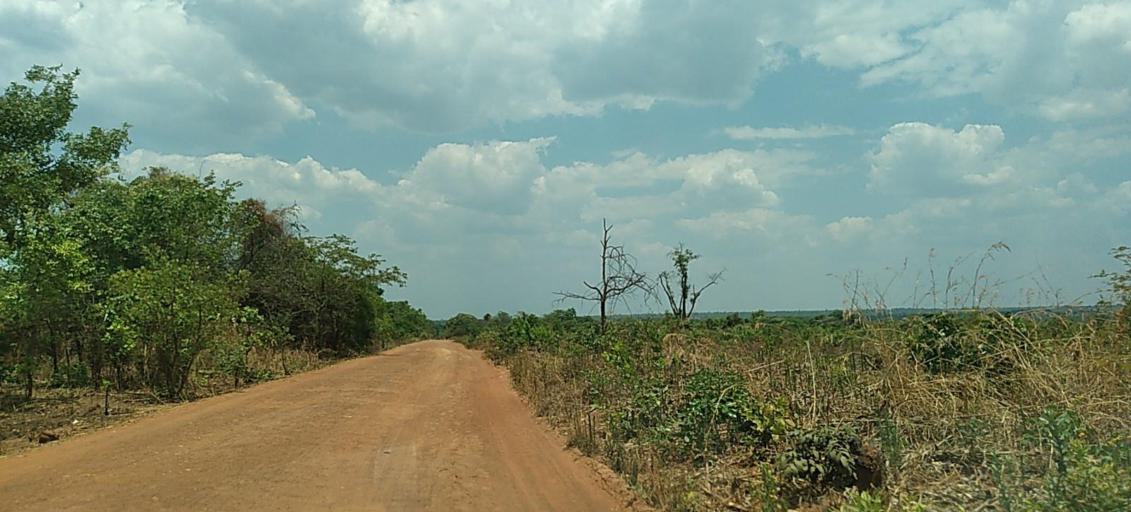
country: ZM
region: Copperbelt
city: Luanshya
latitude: -13.3845
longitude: 28.4406
